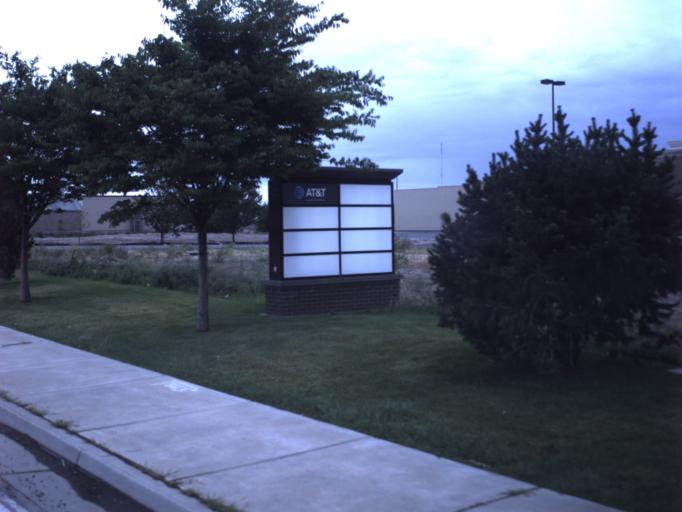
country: US
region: Utah
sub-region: Weber County
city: Ogden
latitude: 41.2431
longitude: -111.9785
